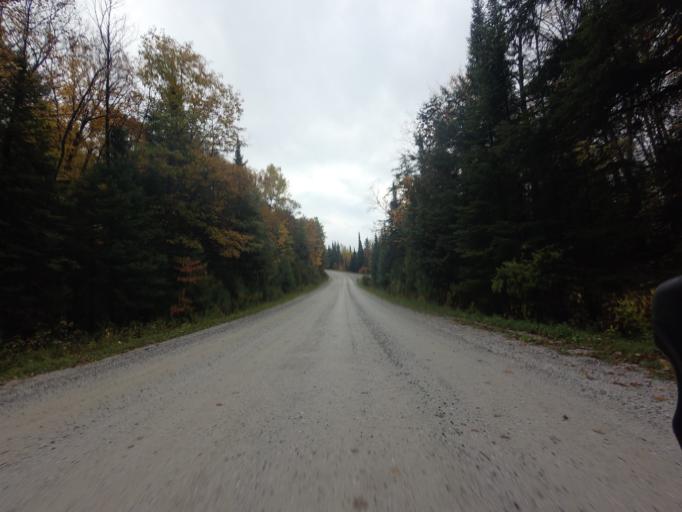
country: CA
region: Ontario
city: Renfrew
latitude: 45.1371
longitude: -76.6657
